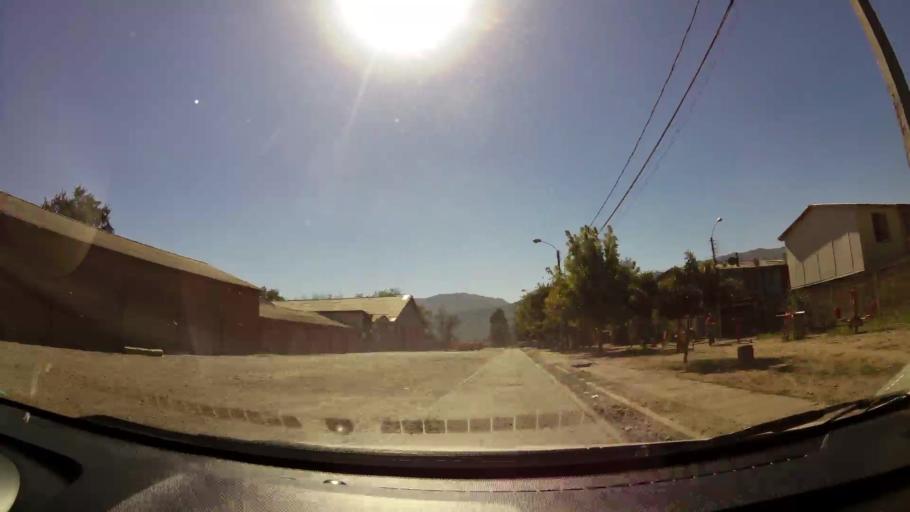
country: CL
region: O'Higgins
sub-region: Provincia de Colchagua
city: Chimbarongo
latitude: -34.5836
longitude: -70.9999
